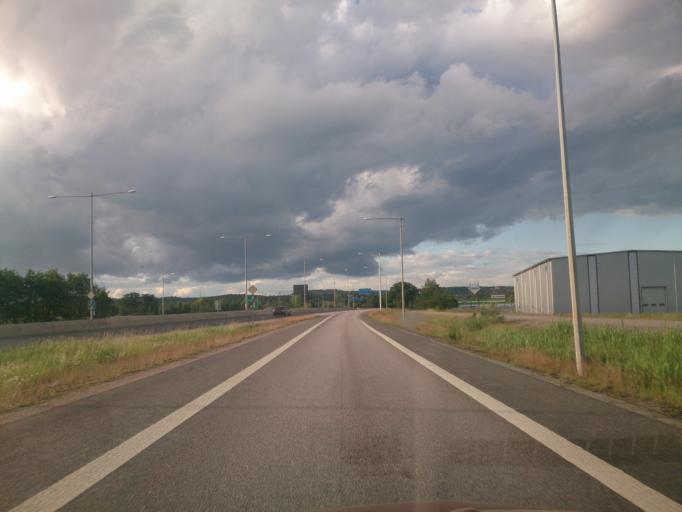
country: SE
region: OEstergoetland
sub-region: Norrkopings Kommun
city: Jursla
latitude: 58.6513
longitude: 16.1683
